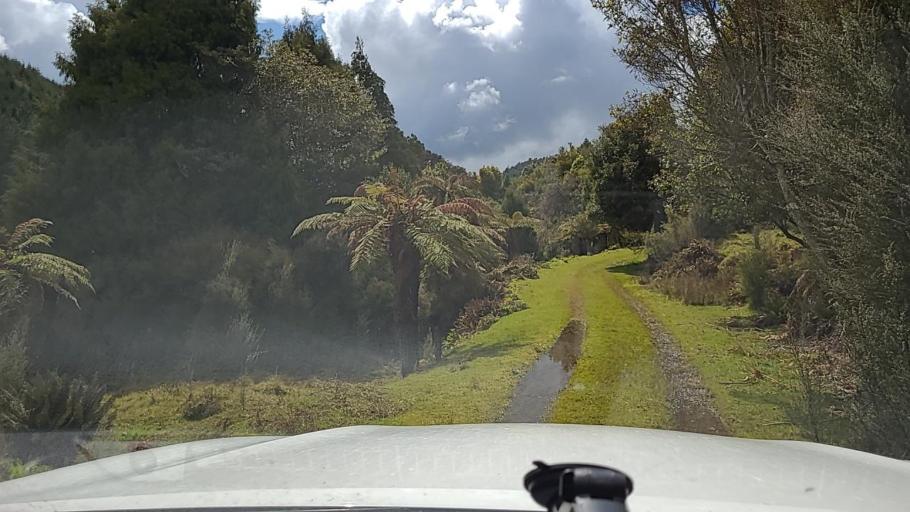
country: NZ
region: Bay of Plenty
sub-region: Opotiki District
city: Opotiki
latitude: -38.2003
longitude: 177.6211
